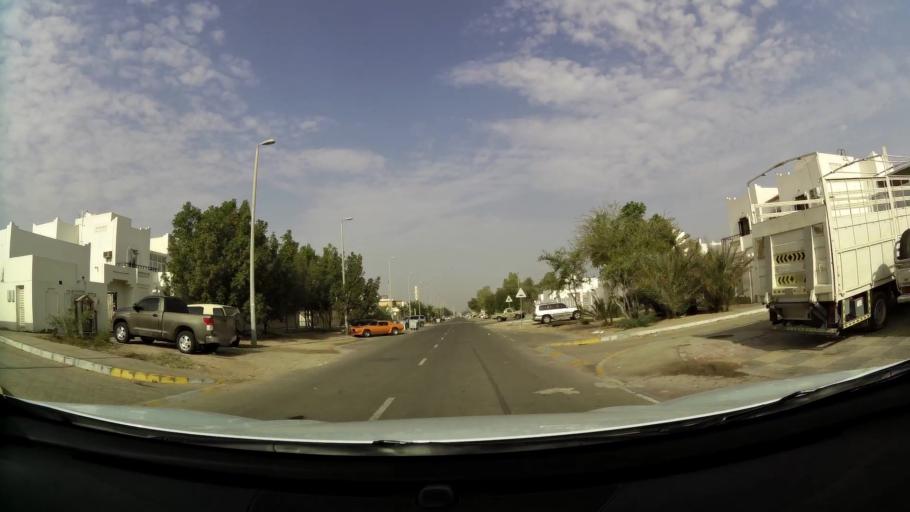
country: AE
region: Abu Dhabi
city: Abu Dhabi
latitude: 24.2395
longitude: 54.7218
